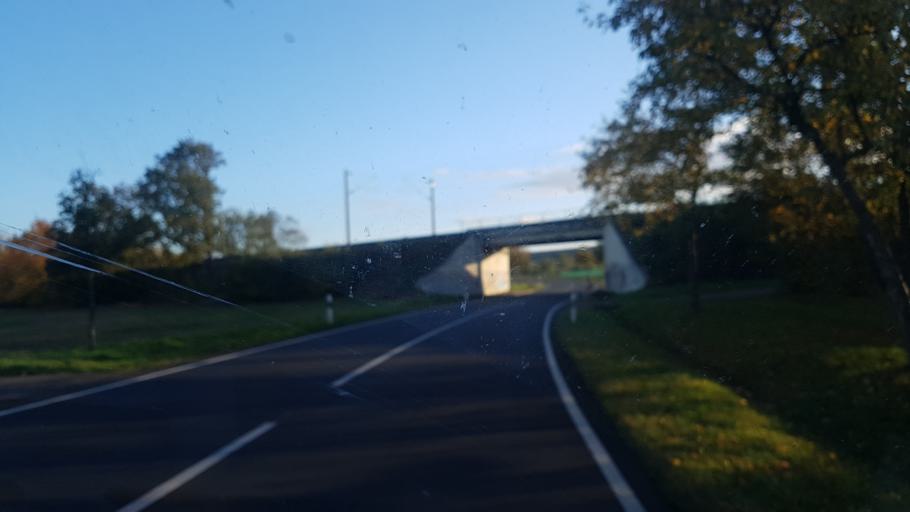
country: DE
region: Saxony
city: Oschatz
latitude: 51.3277
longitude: 13.0547
